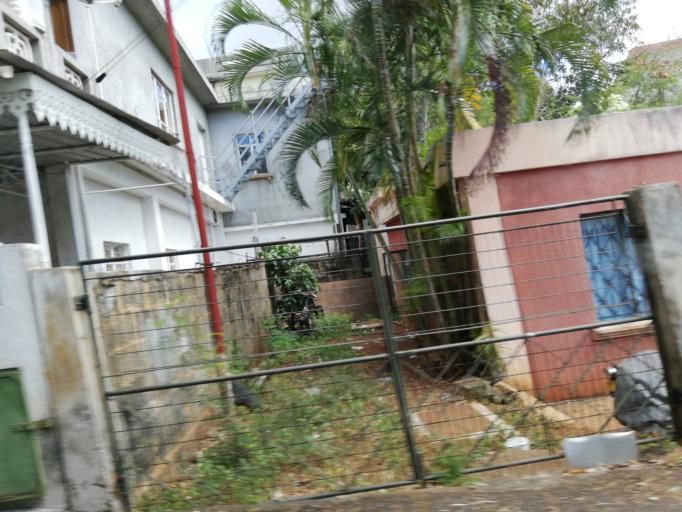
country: MU
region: Moka
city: Pailles
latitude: -20.2045
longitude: 57.4717
